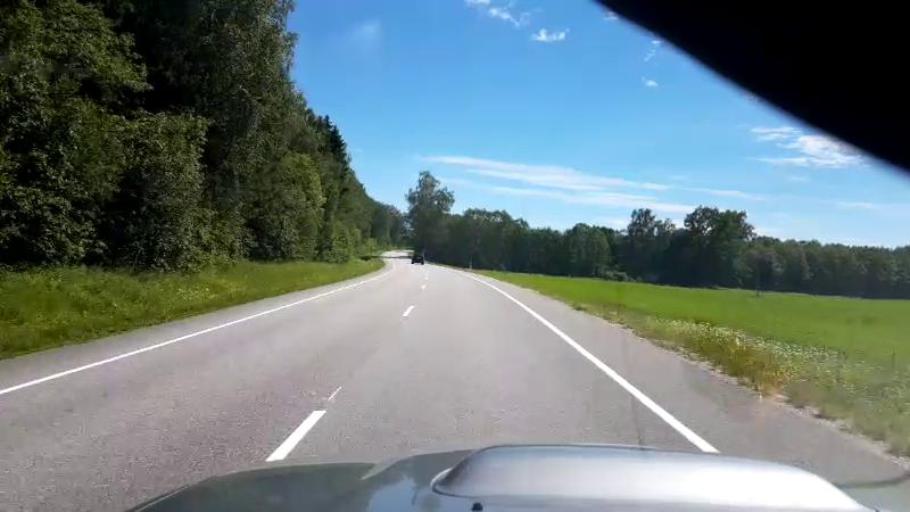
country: EE
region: Jaervamaa
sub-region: Jaerva-Jaani vald
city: Jarva-Jaani
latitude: 59.0117
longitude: 25.9210
